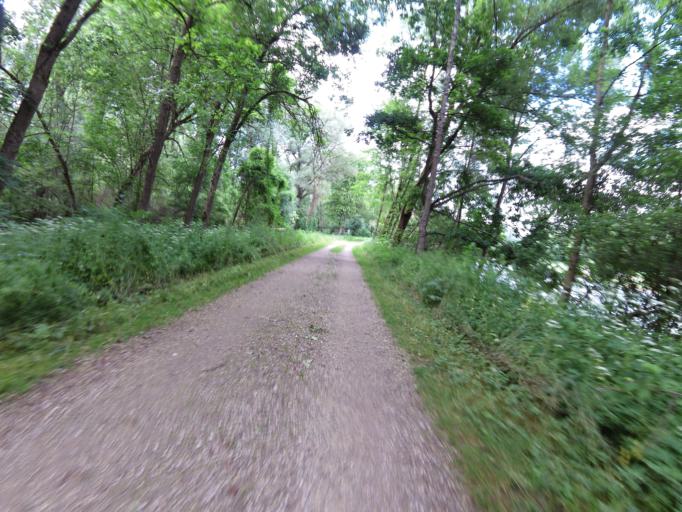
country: DE
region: Bavaria
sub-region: Upper Bavaria
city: Moosburg
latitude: 48.4498
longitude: 11.9419
